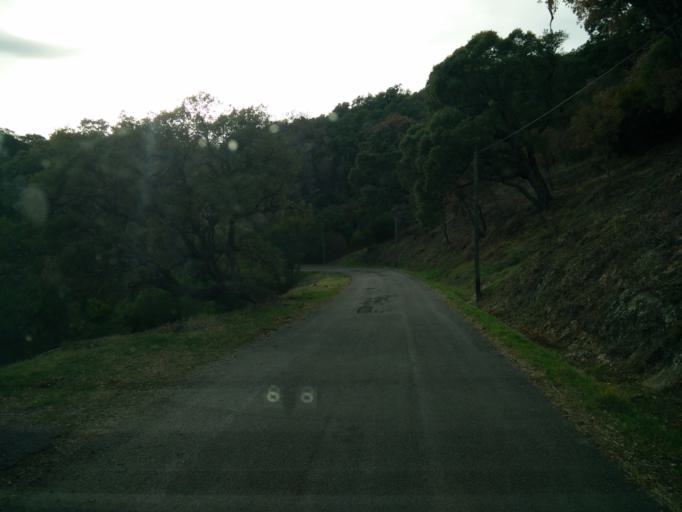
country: FR
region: Provence-Alpes-Cote d'Azur
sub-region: Departement du Var
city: Roquebrune-sur-Argens
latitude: 43.4250
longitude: 6.6379
